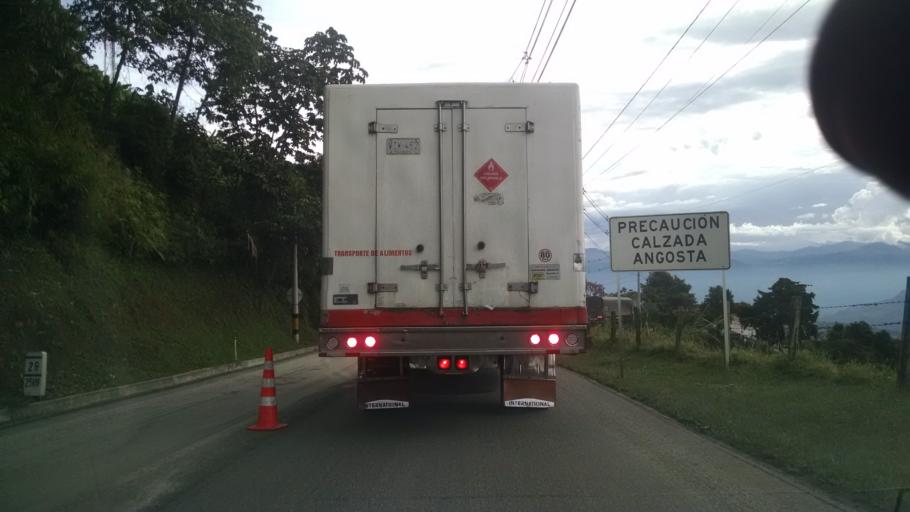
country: CO
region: Antioquia
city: Santa Barbara
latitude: 5.8873
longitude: -75.5722
